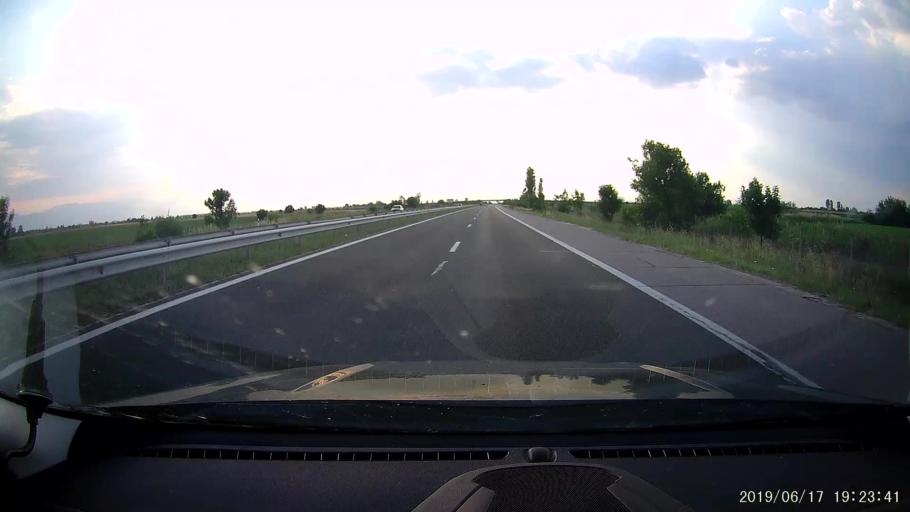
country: BG
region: Pazardzhik
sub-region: Obshtina Pazardzhik
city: Pazardzhik
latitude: 42.2208
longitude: 24.4003
